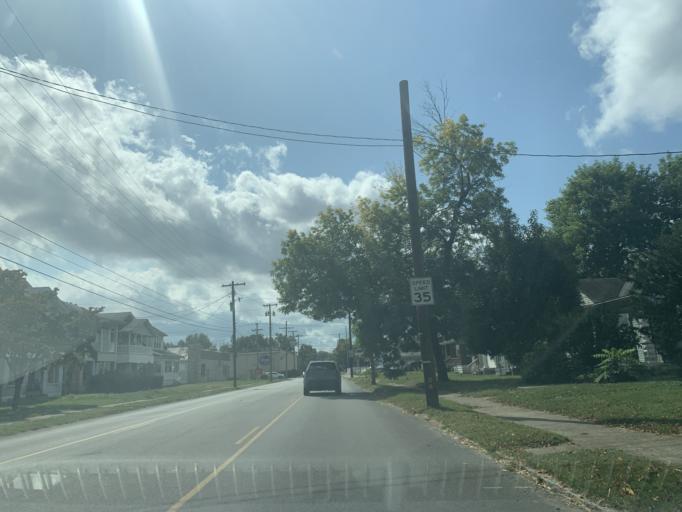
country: US
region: Kentucky
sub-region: Jefferson County
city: Audubon Park
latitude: 38.1965
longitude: -85.7651
